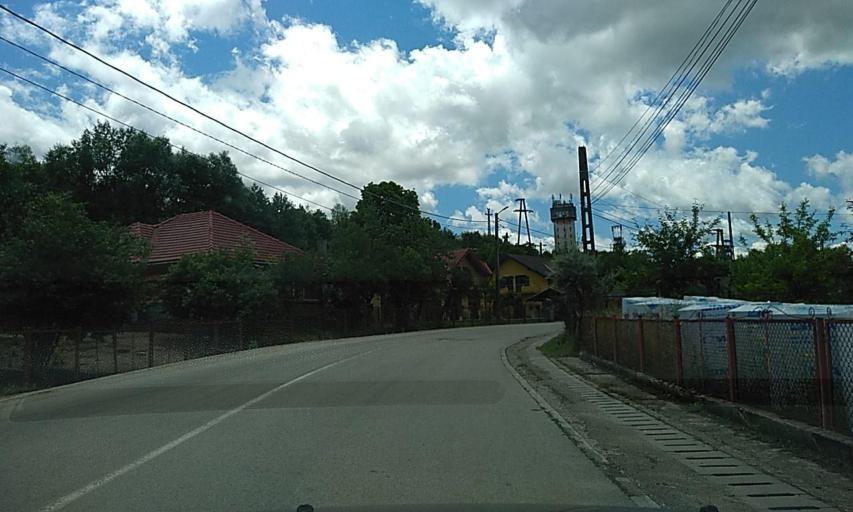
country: RO
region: Hunedoara
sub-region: Oras Petrila
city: Petrila
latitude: 45.4537
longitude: 23.4367
